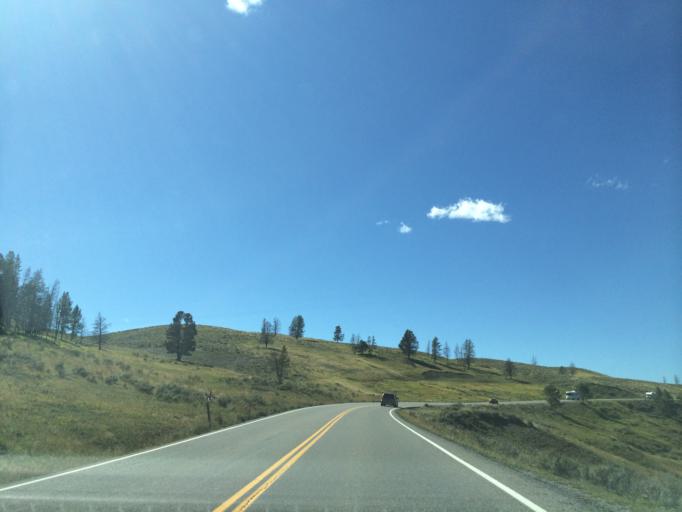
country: US
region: Montana
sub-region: Gallatin County
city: West Yellowstone
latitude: 44.6304
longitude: -110.4411
